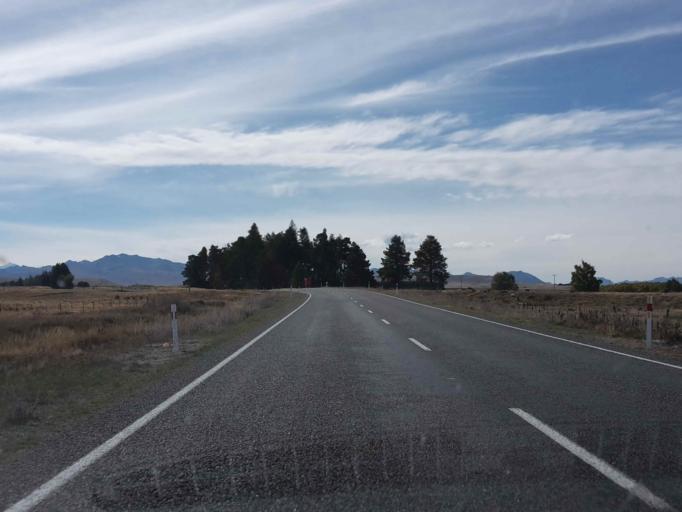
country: NZ
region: Canterbury
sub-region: Timaru District
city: Pleasant Point
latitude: -44.1018
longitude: 170.3541
